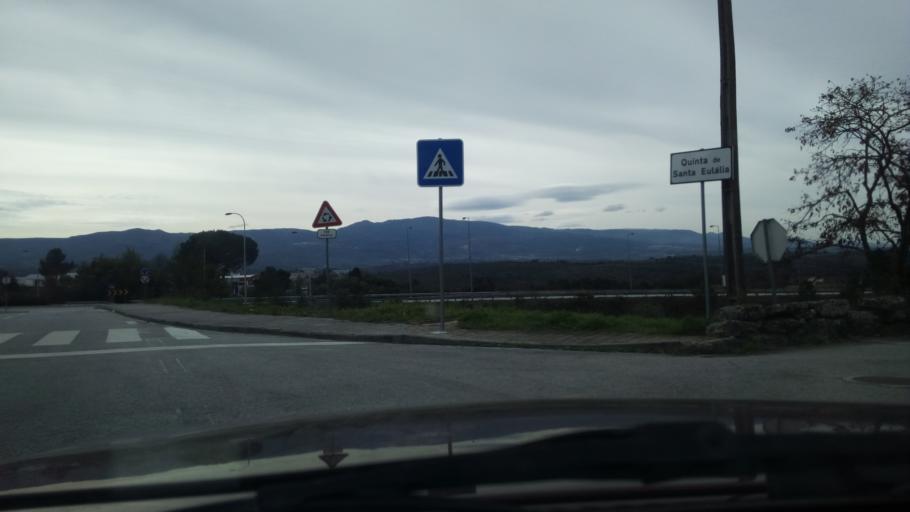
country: PT
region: Guarda
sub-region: Fornos de Algodres
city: Fornos de Algodres
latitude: 40.6151
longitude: -7.5340
